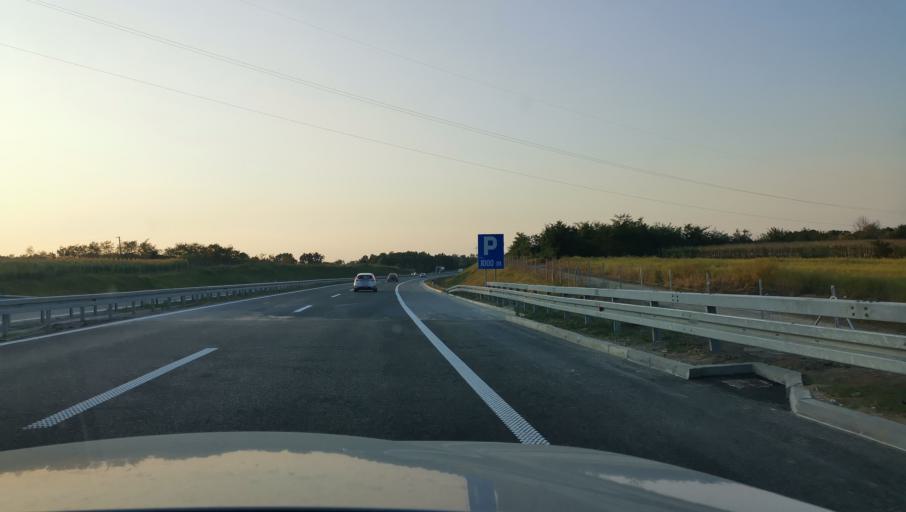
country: RS
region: Central Serbia
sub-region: Kolubarski Okrug
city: Ub
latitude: 44.3955
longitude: 20.0979
